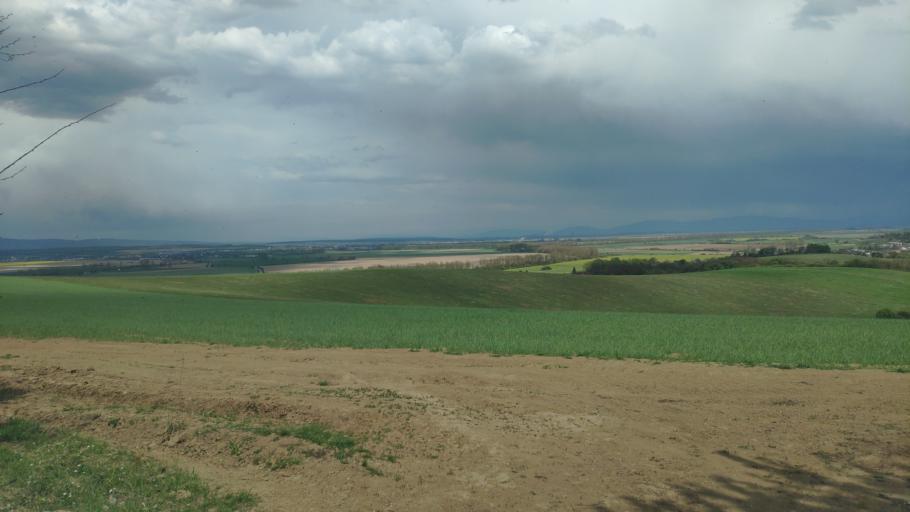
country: SK
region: Kosicky
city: Moldava nad Bodvou
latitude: 48.5566
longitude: 20.9455
